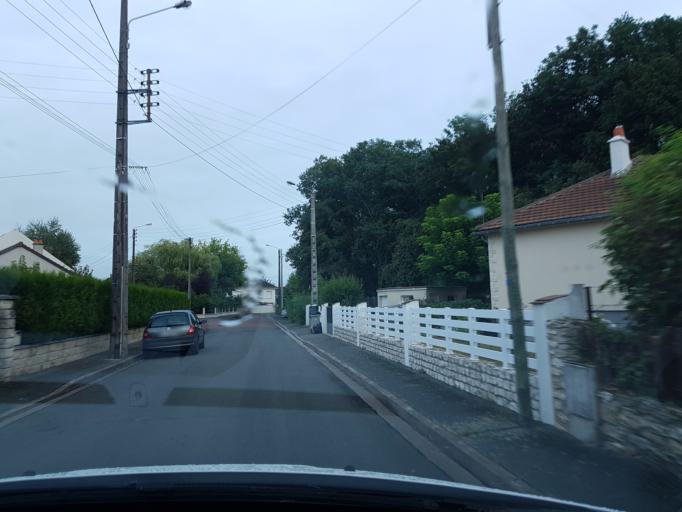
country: FR
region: Centre
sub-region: Departement d'Indre-et-Loire
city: Saint-Avertin
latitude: 47.3668
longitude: 0.7505
